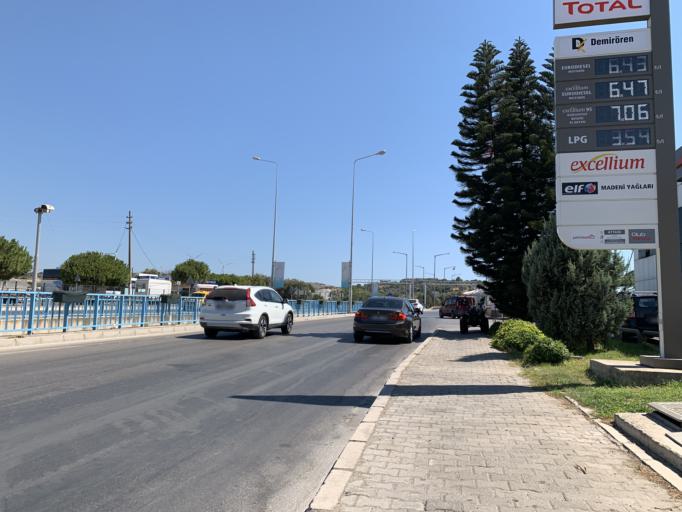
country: TR
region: Izmir
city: Cesme
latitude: 38.3158
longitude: 26.3042
